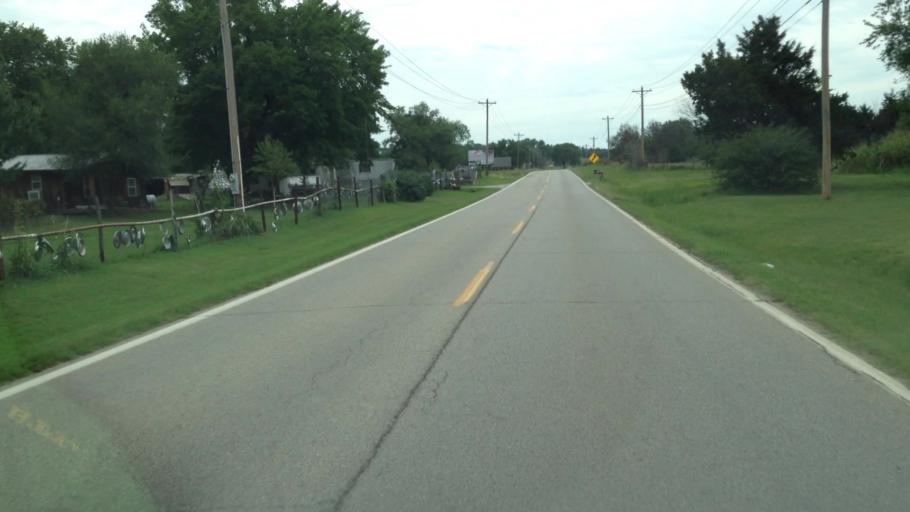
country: US
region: Oklahoma
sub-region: Delaware County
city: Cleora
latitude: 36.5781
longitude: -94.9708
